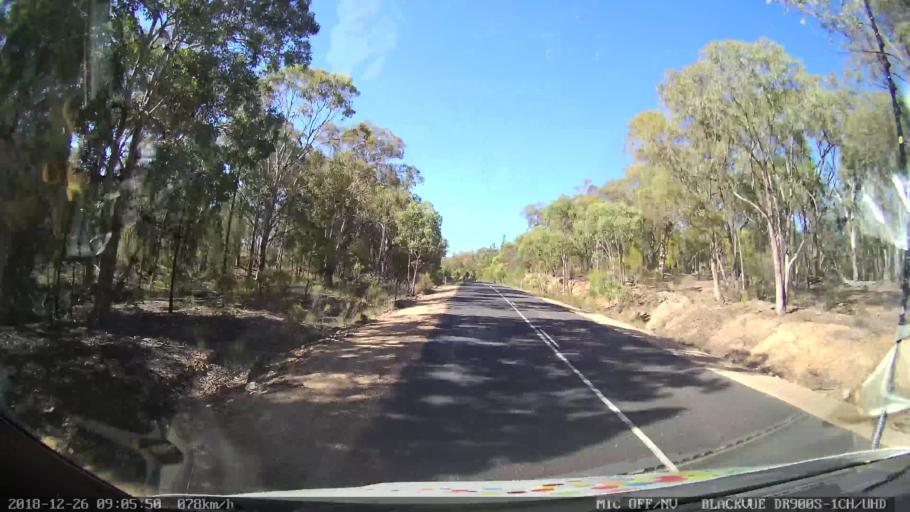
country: AU
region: New South Wales
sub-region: Mid-Western Regional
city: Kandos
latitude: -32.6871
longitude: 150.0053
